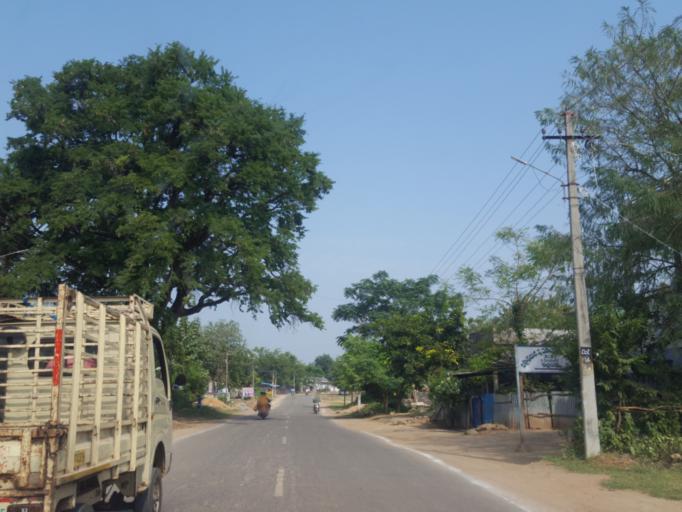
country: IN
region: Telangana
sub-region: Khammam
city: Yellandu
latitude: 17.6021
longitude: 80.3166
